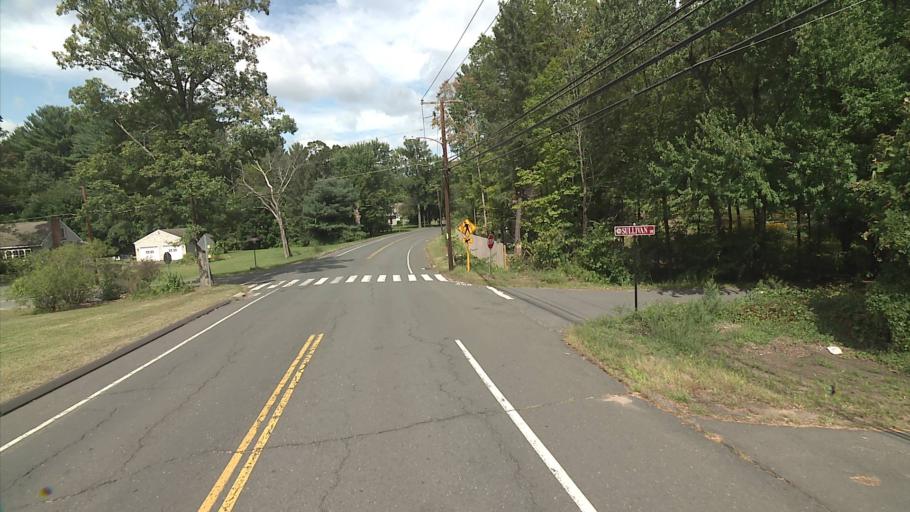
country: US
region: Connecticut
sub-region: Hartford County
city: Salmon Brook
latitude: 41.9623
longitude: -72.8009
